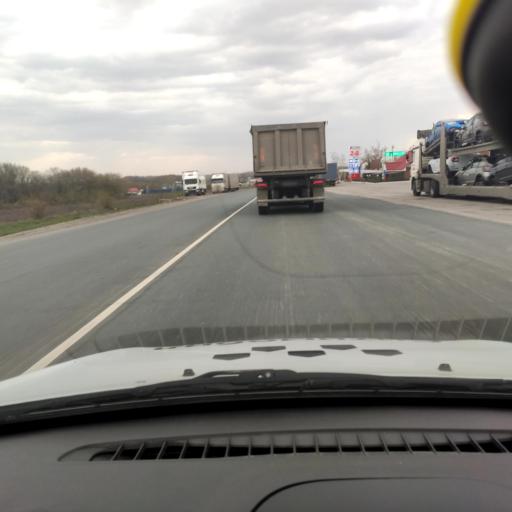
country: RU
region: Samara
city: Zhigulevsk
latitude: 53.3277
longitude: 49.4210
